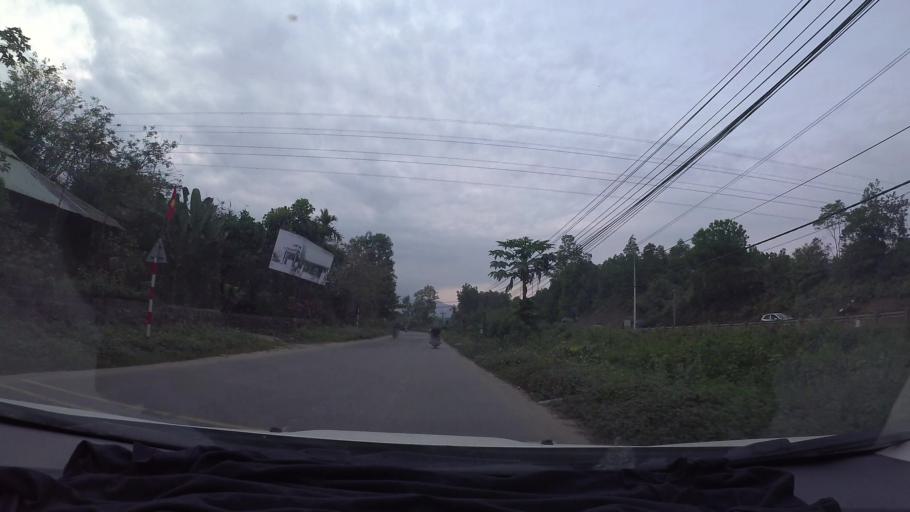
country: VN
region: Da Nang
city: Lien Chieu
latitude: 16.0563
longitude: 108.1004
